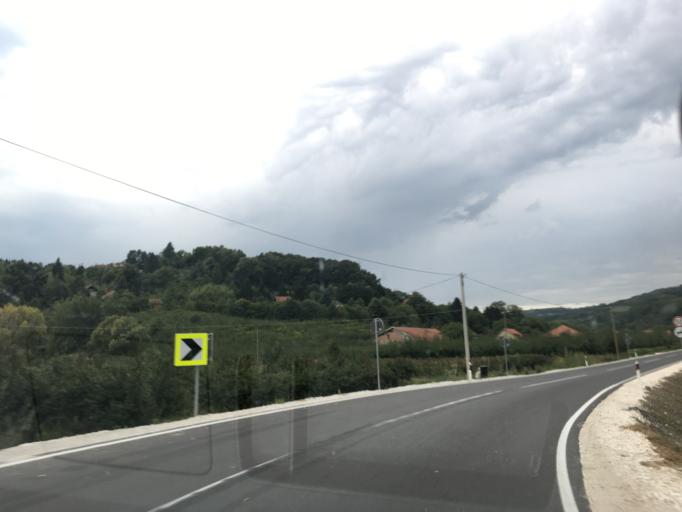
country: RS
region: Central Serbia
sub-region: Sumadijski Okrug
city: Arangelovac
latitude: 44.1865
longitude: 20.5532
